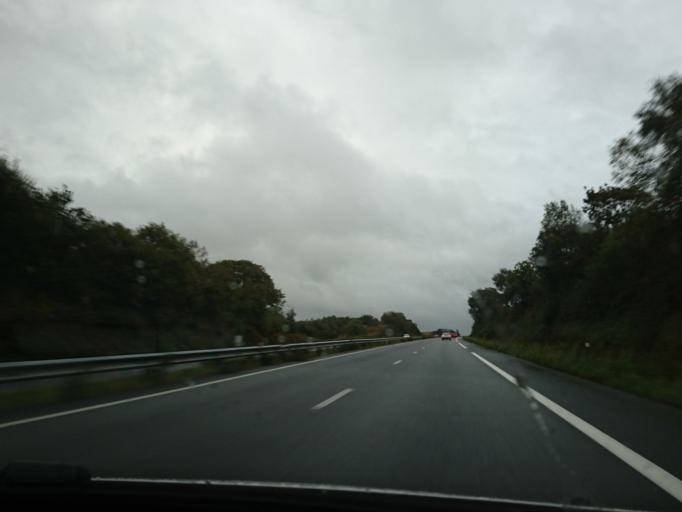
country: FR
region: Brittany
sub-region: Departement du Finistere
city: Daoulas
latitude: 48.3550
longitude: -4.2433
